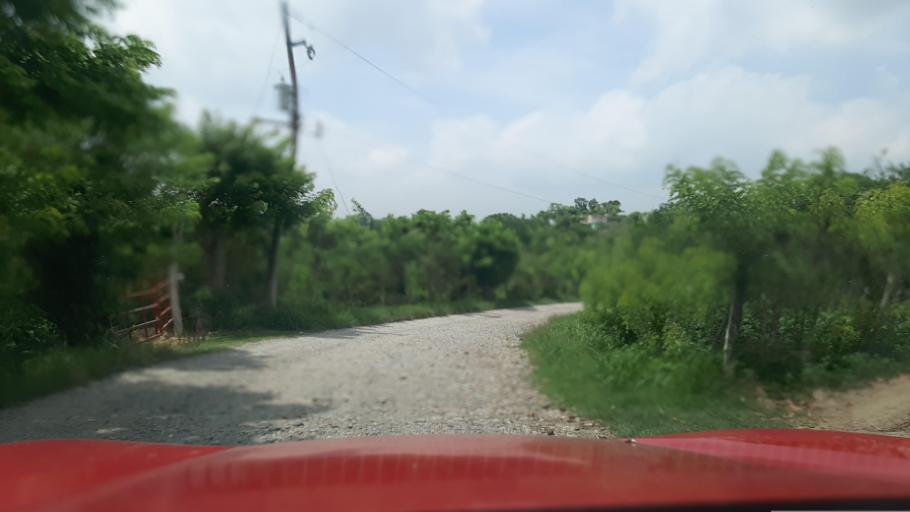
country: MX
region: Veracruz
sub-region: Papantla
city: Polutla
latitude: 20.4577
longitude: -97.2400
